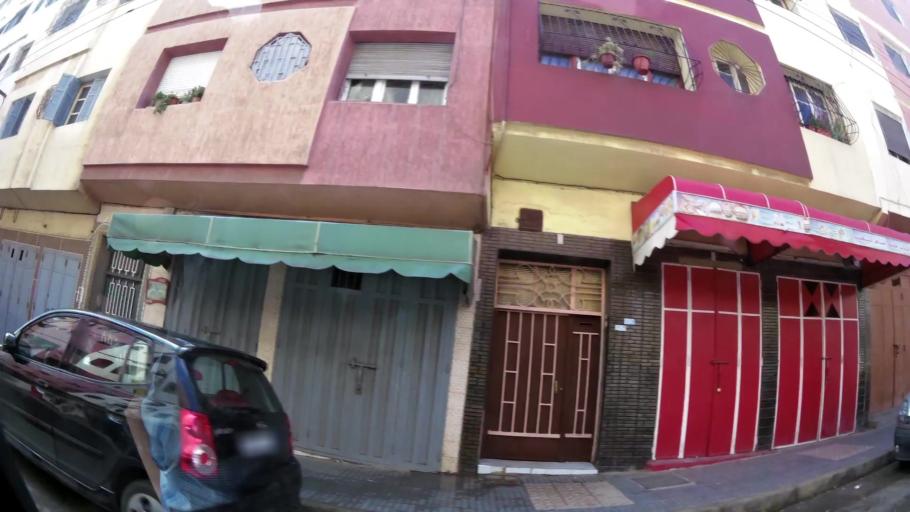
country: MA
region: Grand Casablanca
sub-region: Casablanca
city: Casablanca
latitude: 33.5738
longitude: -7.5837
